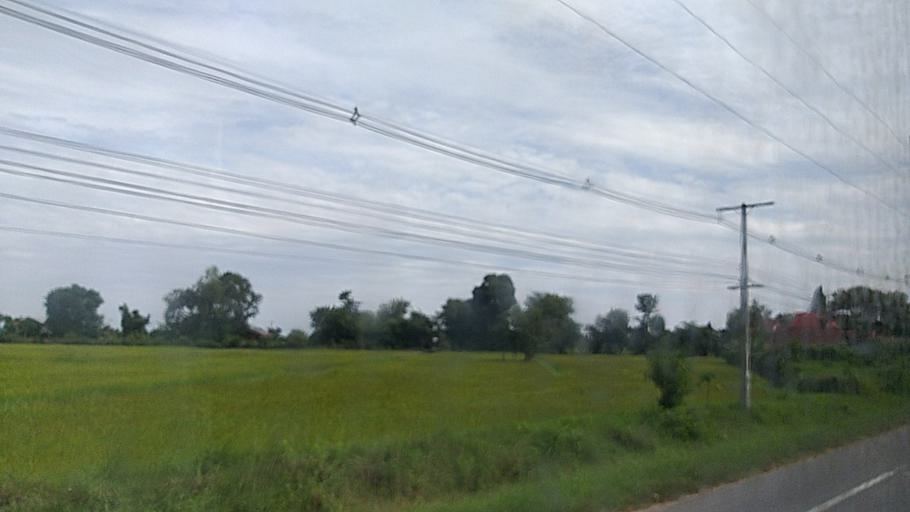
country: TH
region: Maha Sarakham
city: Chiang Yuen
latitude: 16.4241
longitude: 103.0703
